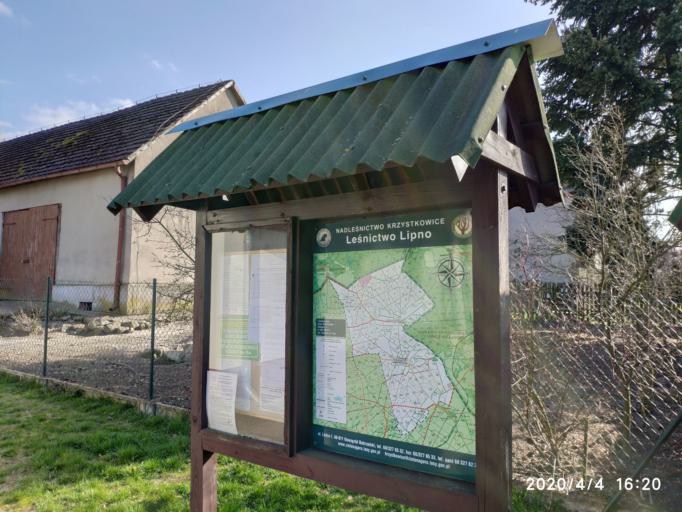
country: PL
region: Lubusz
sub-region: Powiat zielonogorski
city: Swidnica
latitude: 51.8953
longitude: 15.2827
